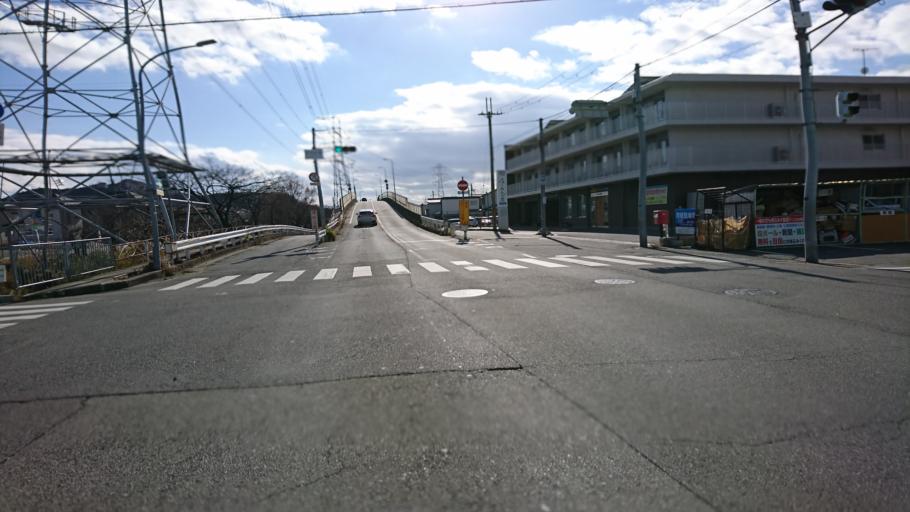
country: JP
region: Hyogo
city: Kakogawacho-honmachi
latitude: 34.7940
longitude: 134.7839
